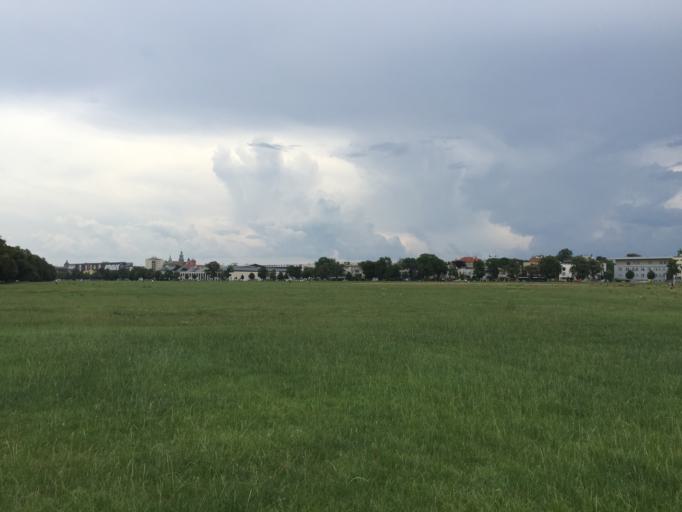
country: PL
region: Lesser Poland Voivodeship
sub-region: Krakow
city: Krakow
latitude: 50.0606
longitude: 19.9118
